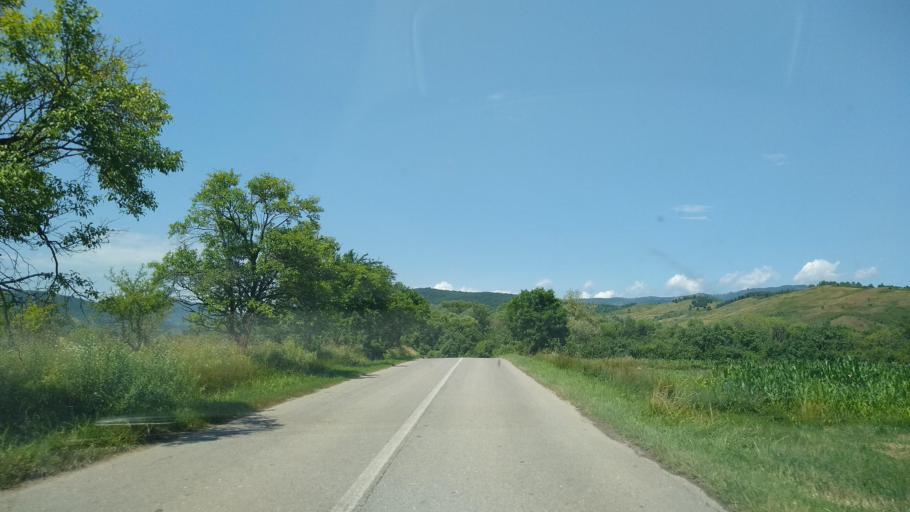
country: RO
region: Hunedoara
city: Densus
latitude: 45.5790
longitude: 22.8220
